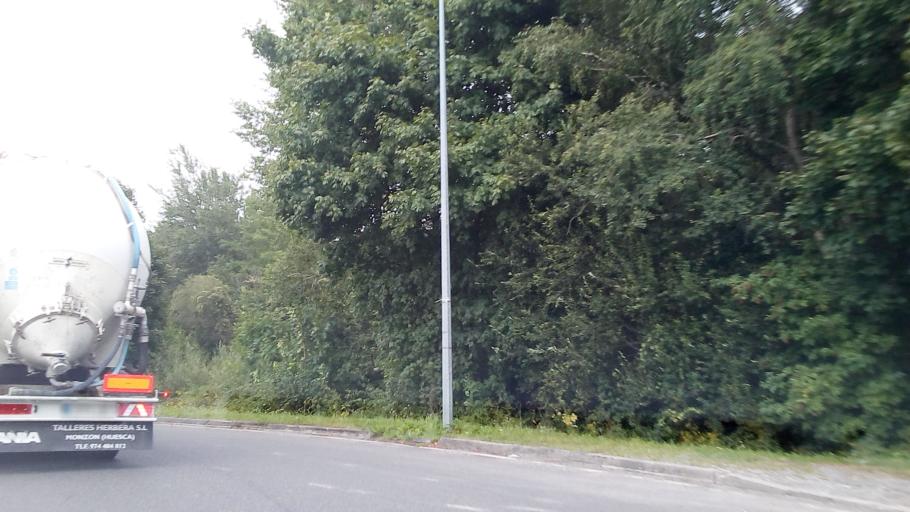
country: FR
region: Midi-Pyrenees
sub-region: Departement des Hautes-Pyrenees
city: La Barthe-de-Neste
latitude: 43.0960
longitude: 0.3900
